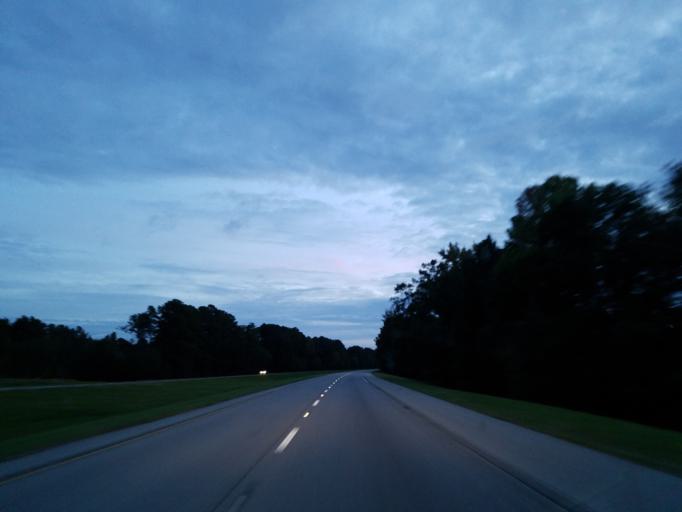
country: US
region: Mississippi
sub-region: Clarke County
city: Stonewall
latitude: 32.1415
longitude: -88.8698
